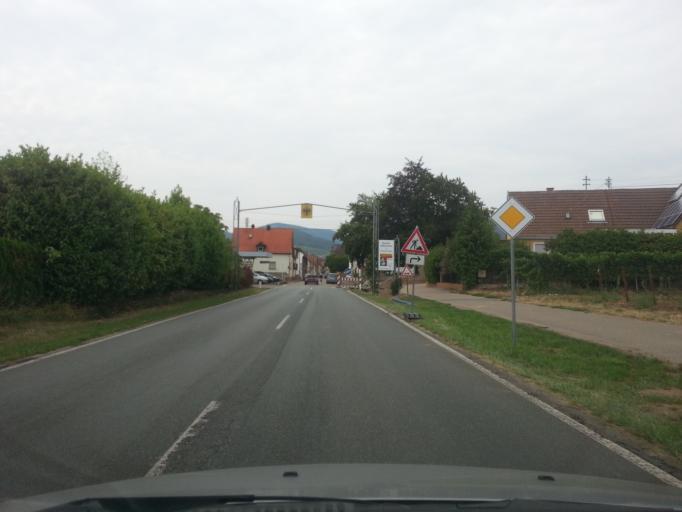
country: DE
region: Rheinland-Pfalz
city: Siebeldingen
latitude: 49.2111
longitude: 8.0568
